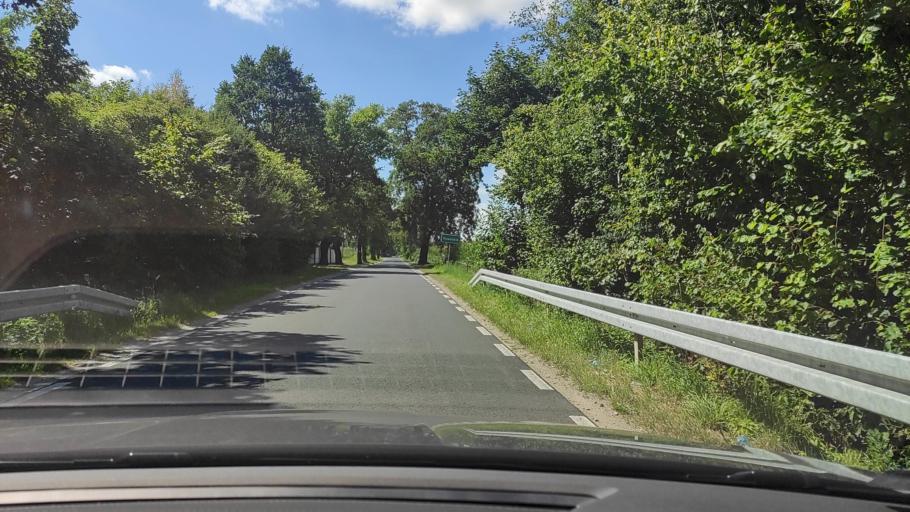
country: PL
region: Greater Poland Voivodeship
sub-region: Powiat poznanski
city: Kobylnica
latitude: 52.4816
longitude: 17.1695
